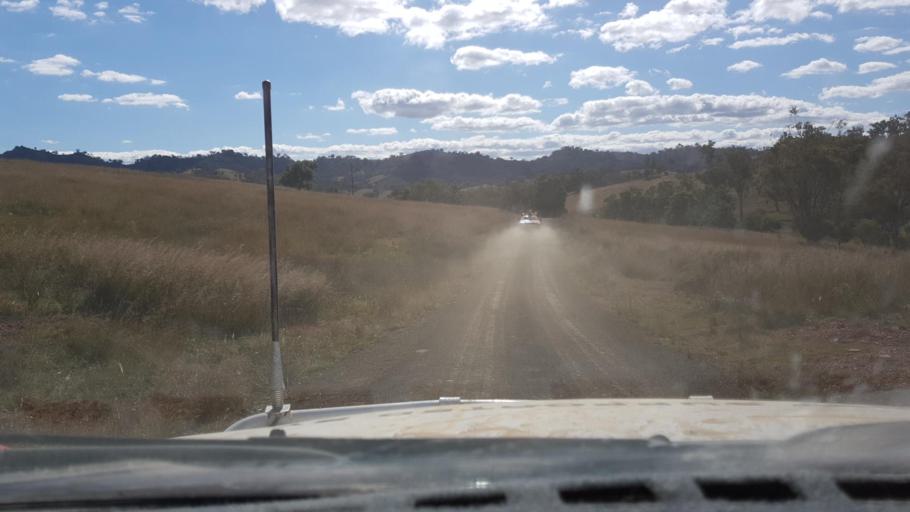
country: AU
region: New South Wales
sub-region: Tamworth Municipality
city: Manilla
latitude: -30.4560
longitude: 150.7814
